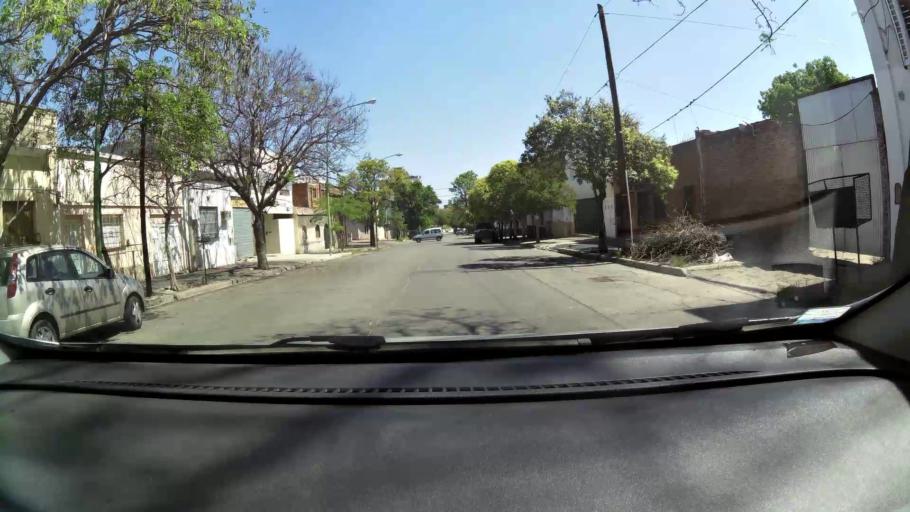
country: AR
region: Cordoba
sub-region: Departamento de Capital
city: Cordoba
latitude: -31.3970
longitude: -64.1922
